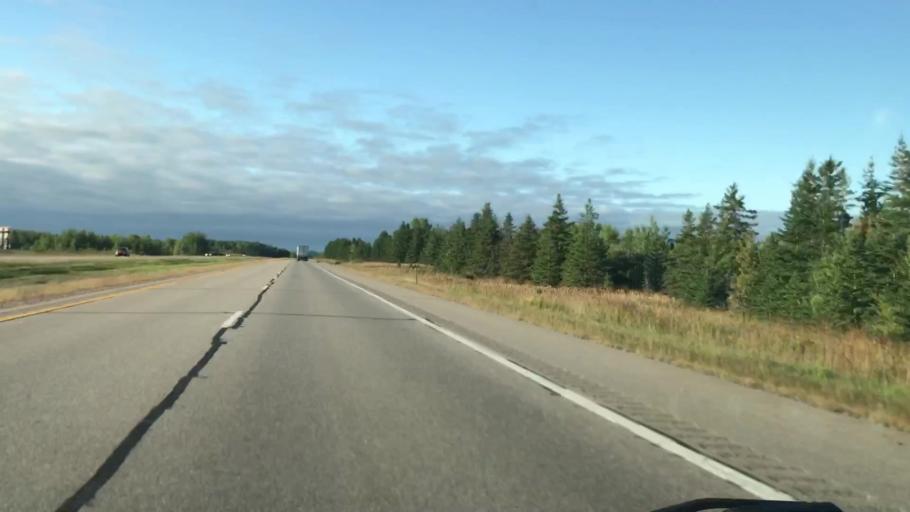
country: US
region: Michigan
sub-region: Chippewa County
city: Sault Ste. Marie
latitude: 46.4002
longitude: -84.4030
